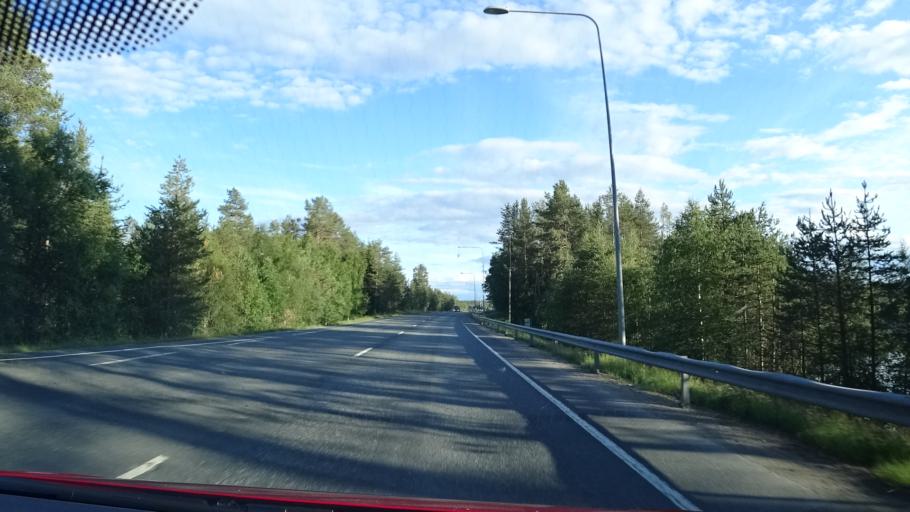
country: FI
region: Northern Ostrobothnia
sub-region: Koillismaa
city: Kuusamo
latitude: 66.0056
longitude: 29.1527
